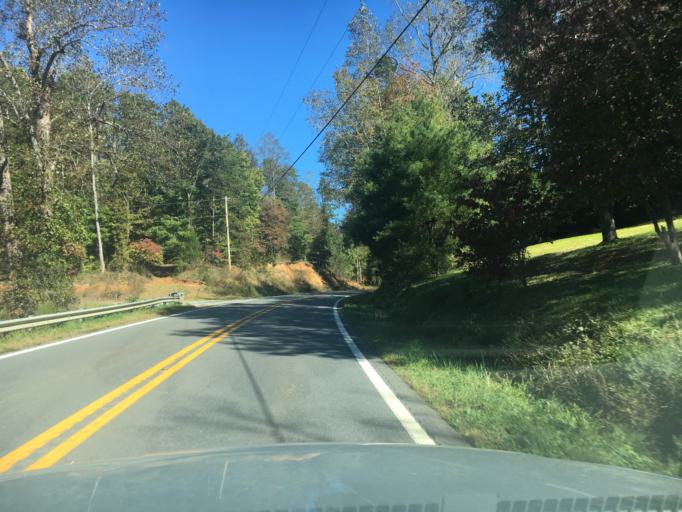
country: US
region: North Carolina
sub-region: Rutherford County
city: Spindale
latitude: 35.4995
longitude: -81.8648
